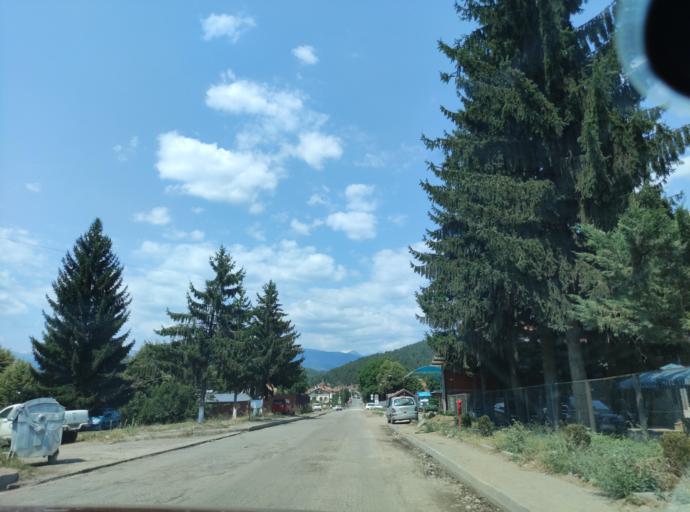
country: BG
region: Blagoevgrad
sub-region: Obshtina Belitsa
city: Belitsa
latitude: 41.9431
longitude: 23.5660
